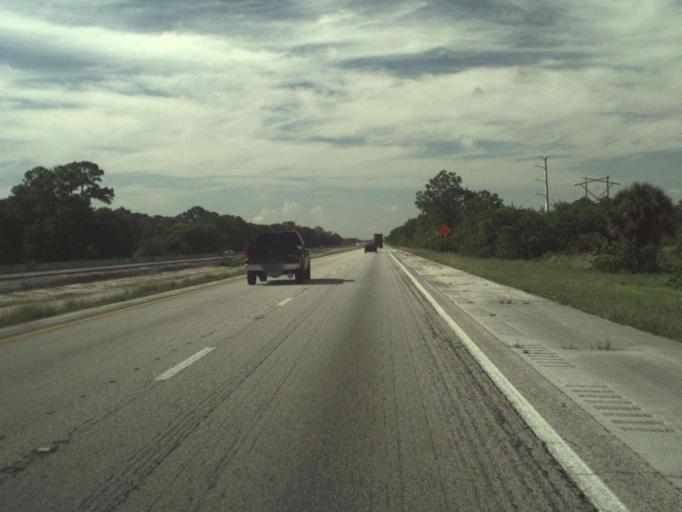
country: US
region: Florida
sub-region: Indian River County
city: West Vero Corridor
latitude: 27.6974
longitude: -80.5392
